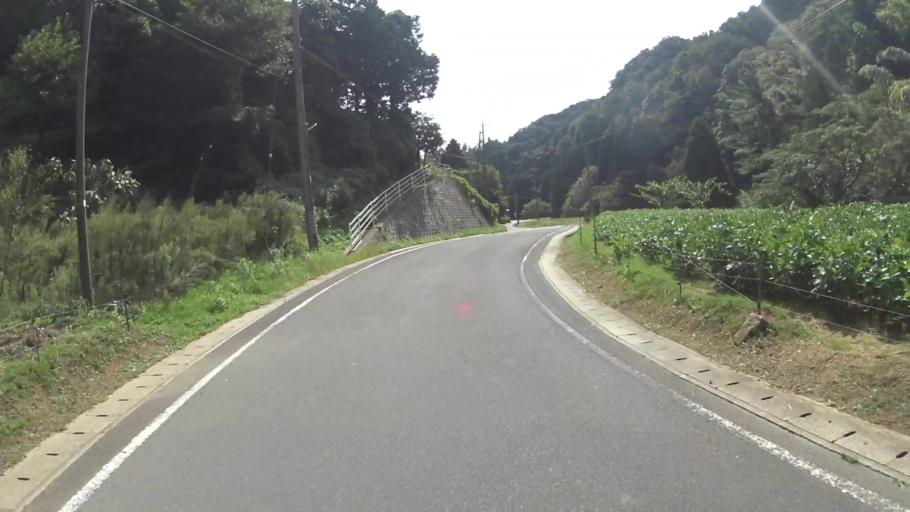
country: JP
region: Kyoto
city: Miyazu
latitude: 35.6694
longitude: 135.2460
